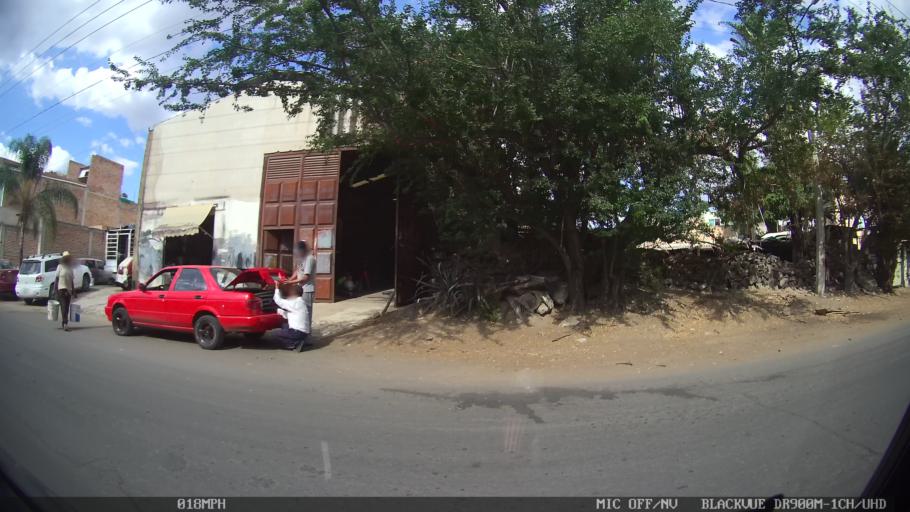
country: MX
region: Jalisco
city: Tlaquepaque
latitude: 20.6625
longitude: -103.2674
